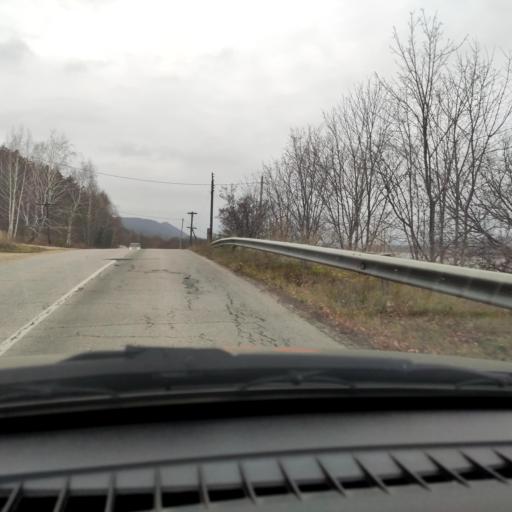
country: RU
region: Samara
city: Pribrezhnyy
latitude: 53.4414
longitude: 49.7605
